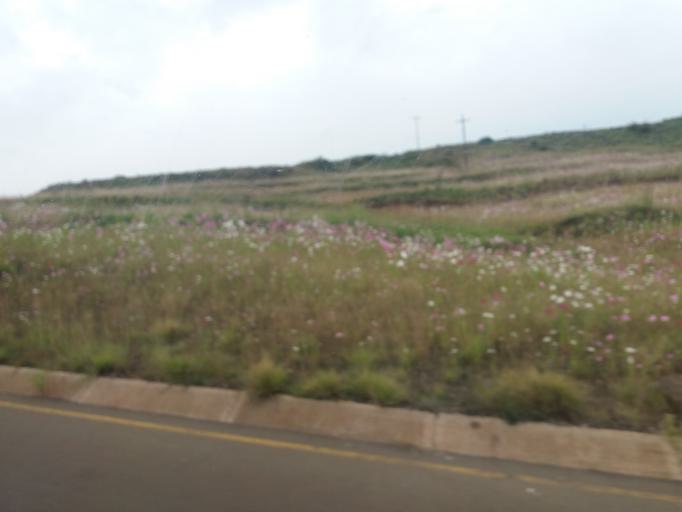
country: LS
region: Berea
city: Teyateyaneng
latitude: -29.3241
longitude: 27.7520
